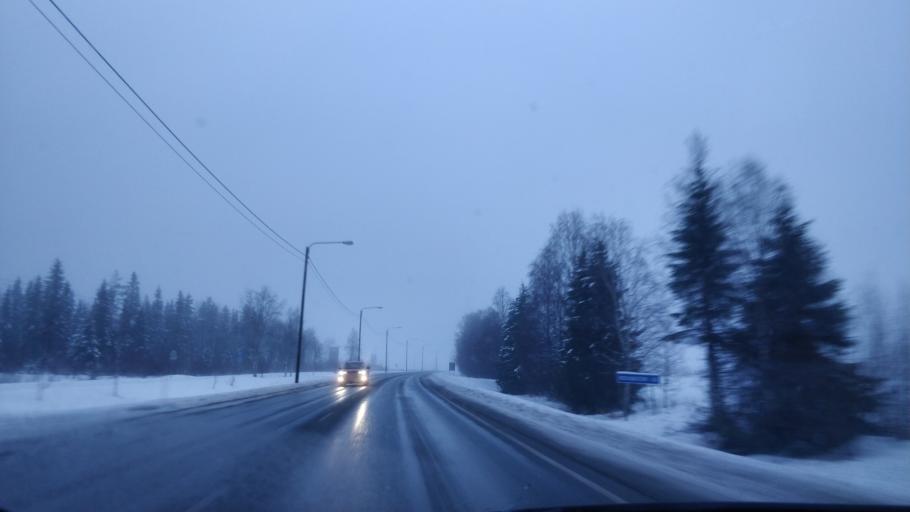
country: FI
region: Lapland
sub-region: Kemi-Tornio
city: Tervola
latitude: 66.1497
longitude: 24.9765
